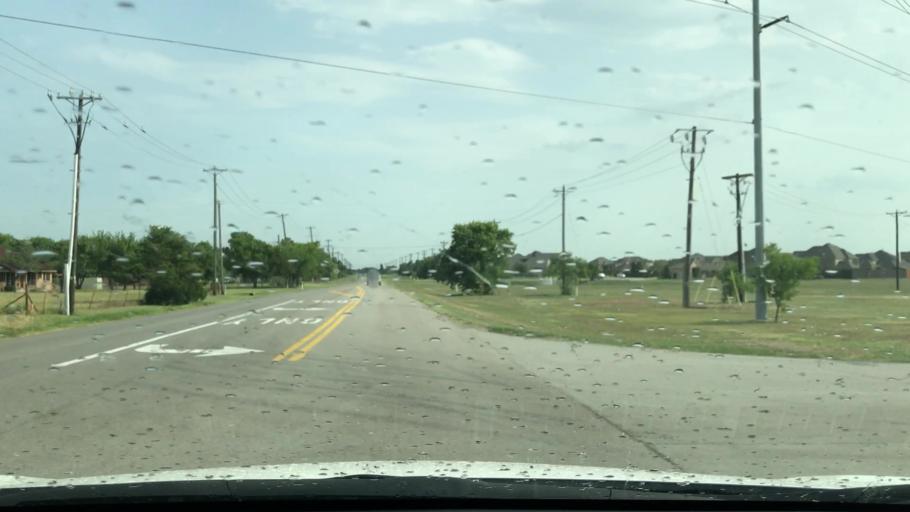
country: US
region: Texas
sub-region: Collin County
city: Wylie
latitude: 32.9915
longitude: -96.5216
